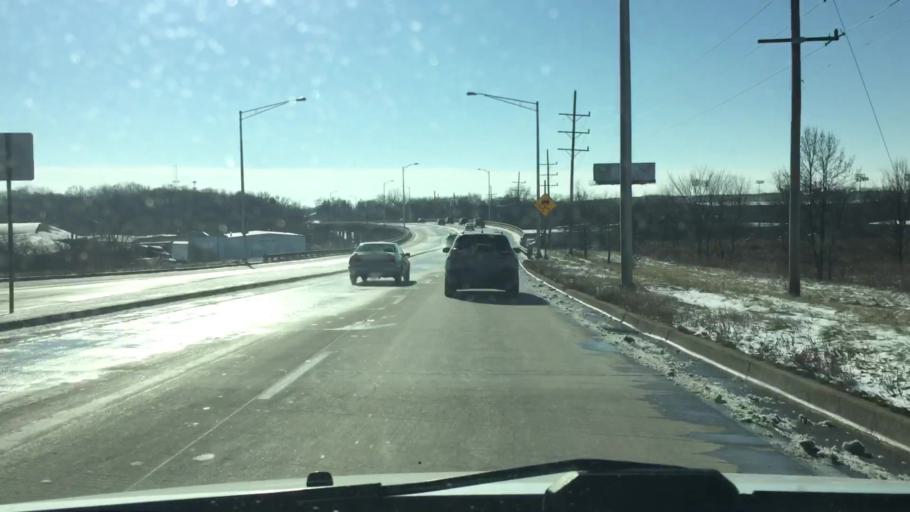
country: US
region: Illinois
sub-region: Kane County
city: Geneva
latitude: 41.8852
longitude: -88.2775
